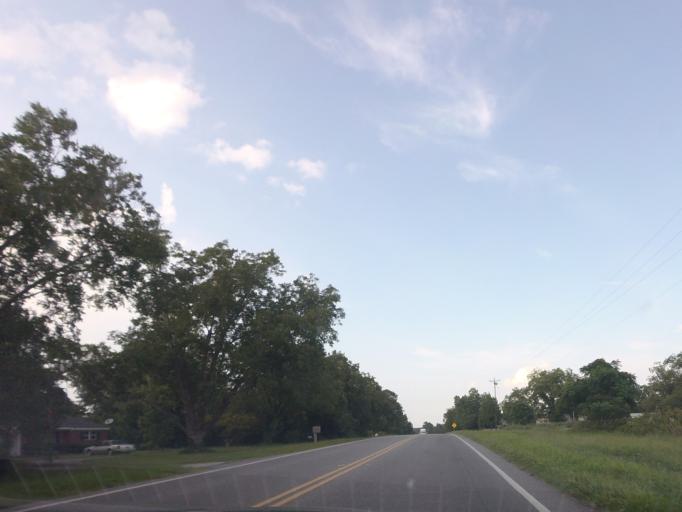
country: US
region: Georgia
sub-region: Bleckley County
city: Cochran
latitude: 32.4208
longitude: -83.3143
